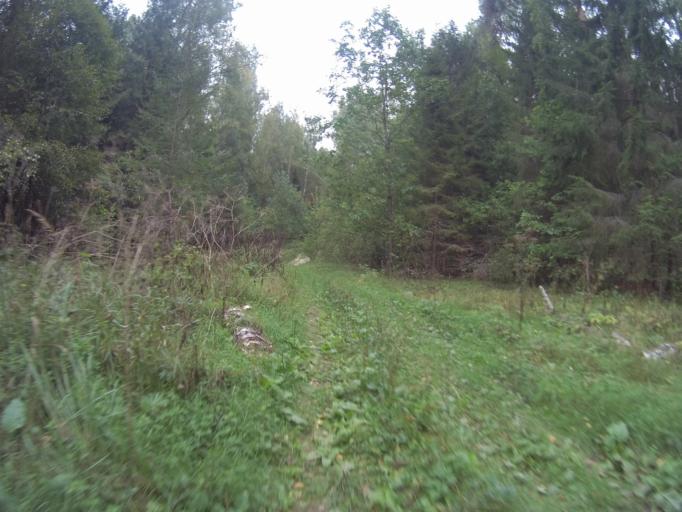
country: RU
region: Vladimir
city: Golovino
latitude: 56.0054
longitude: 40.4924
